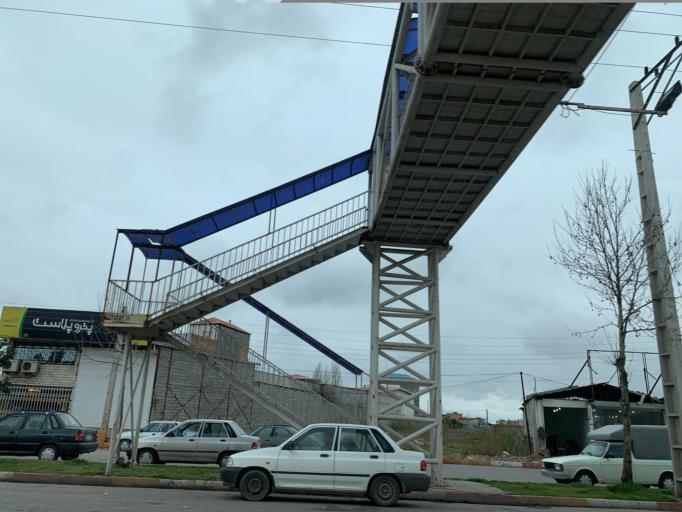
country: IR
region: Mazandaran
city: Babol
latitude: 36.5168
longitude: 52.5766
